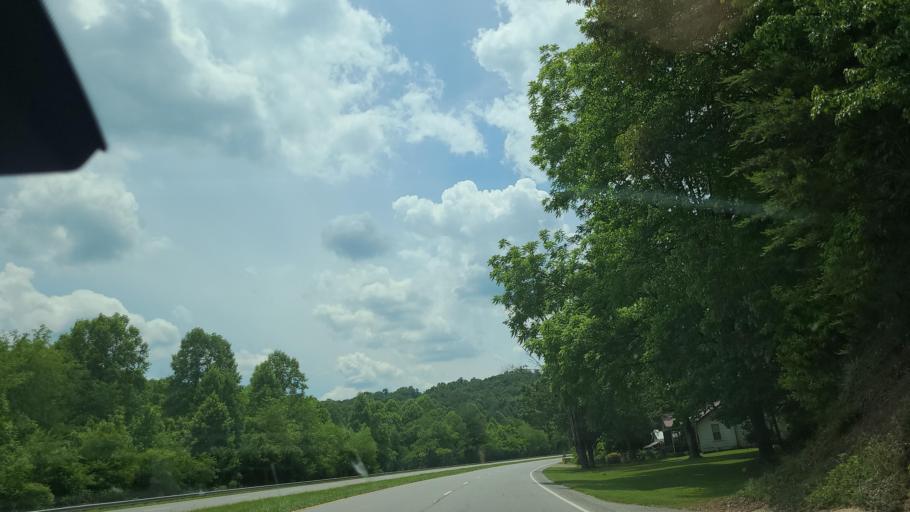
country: US
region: Georgia
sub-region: Fannin County
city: McCaysville
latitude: 35.0254
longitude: -84.2182
